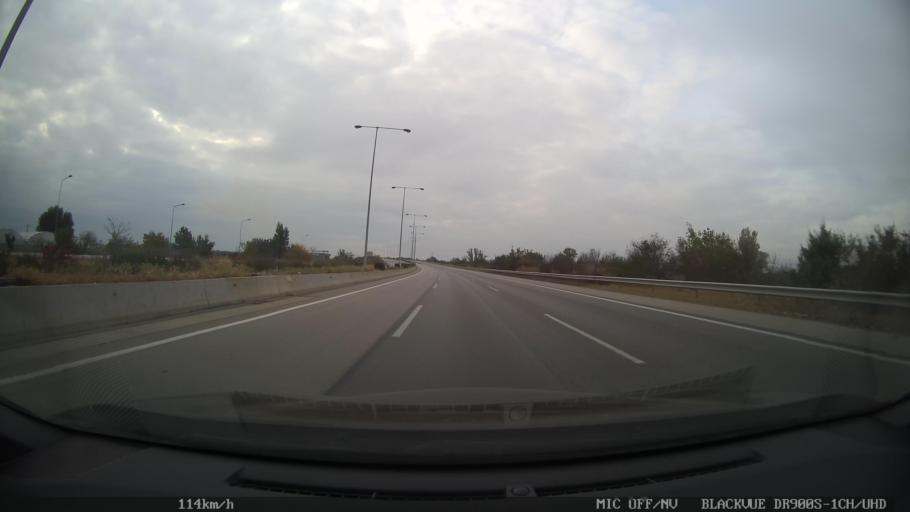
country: GR
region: Central Macedonia
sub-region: Nomos Thessalonikis
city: Nea Magnisia
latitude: 40.6746
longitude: 22.8324
